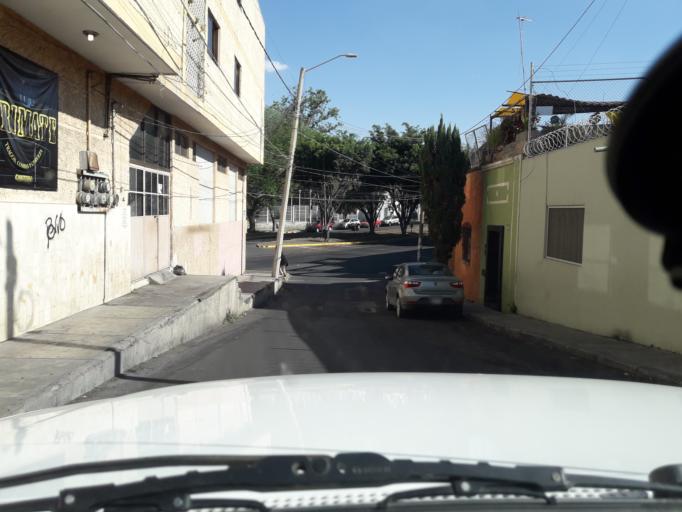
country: MX
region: Jalisco
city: Guadalajara
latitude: 20.6901
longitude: -103.3523
